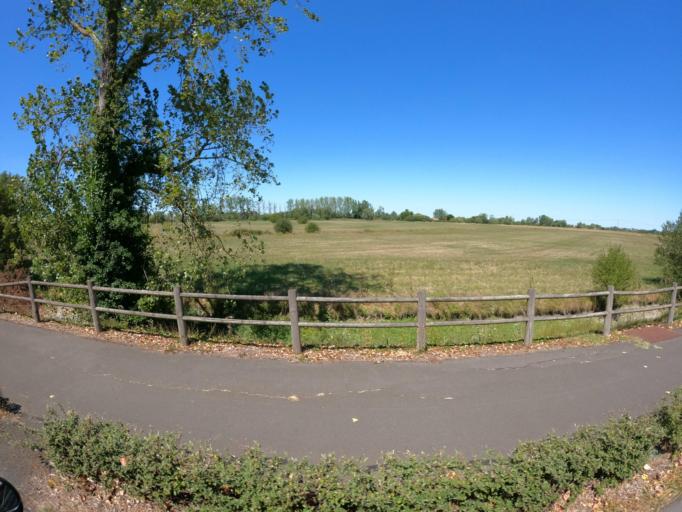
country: FR
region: Pays de la Loire
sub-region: Departement de la Vendee
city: Le Perrier
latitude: 46.8213
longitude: -1.9811
